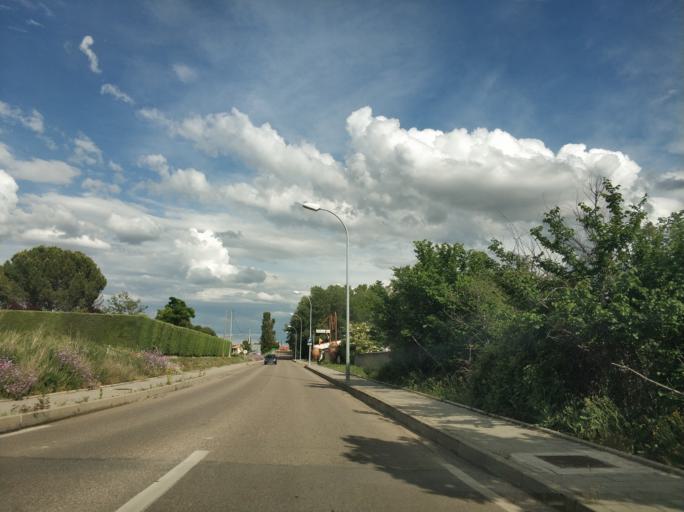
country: ES
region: Castille and Leon
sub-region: Provincia de Burgos
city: Aranda de Duero
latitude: 41.6754
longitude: -3.6989
